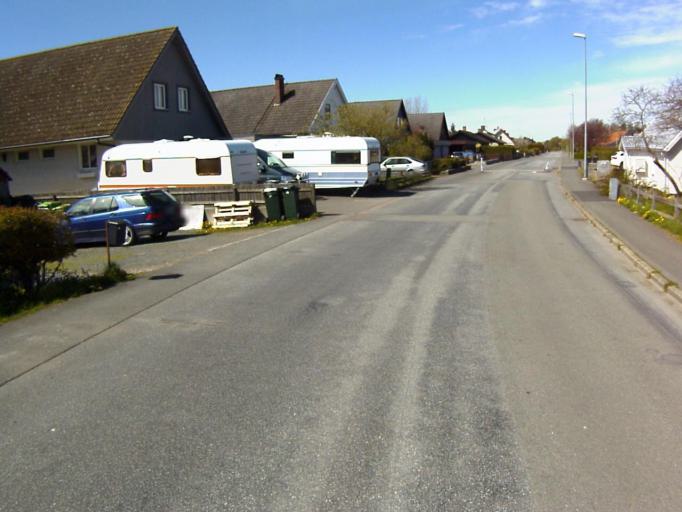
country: SE
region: Skane
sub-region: Kristianstads Kommun
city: Norra Asum
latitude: 55.9989
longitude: 14.1496
